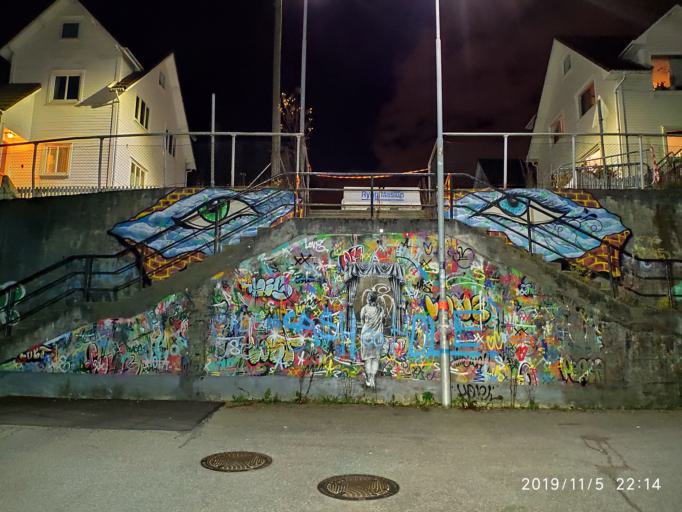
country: NO
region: Rogaland
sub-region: Stavanger
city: Stavanger
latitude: 58.9671
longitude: 5.7529
